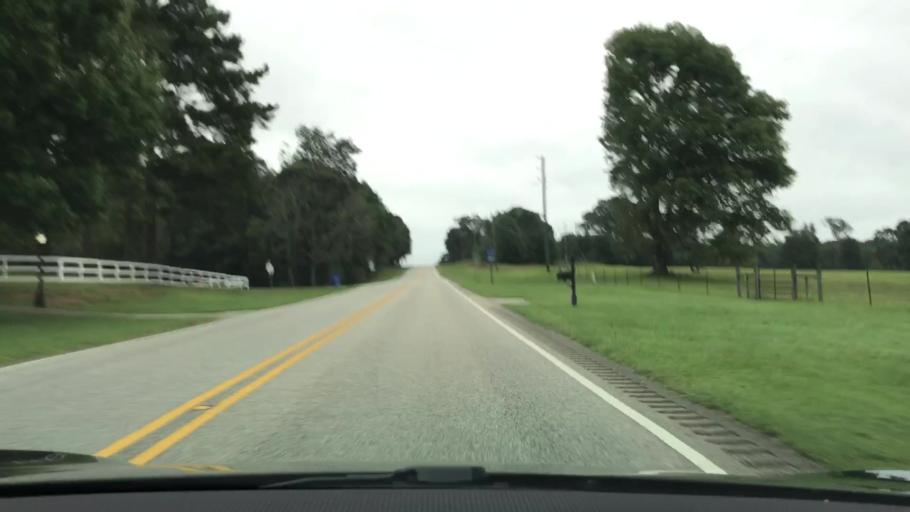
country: US
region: Alabama
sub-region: Coffee County
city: Elba
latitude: 31.3621
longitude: -86.1153
